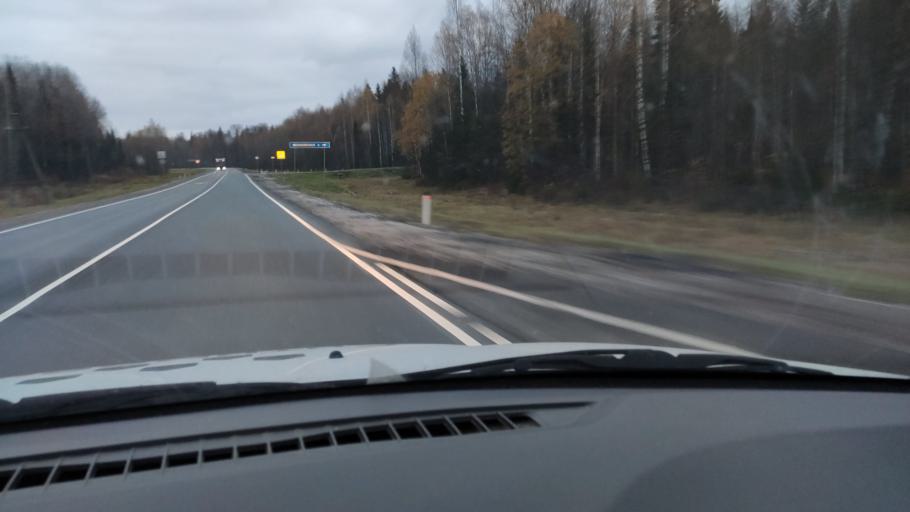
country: RU
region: Kirov
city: Kostino
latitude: 58.8395
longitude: 53.0669
